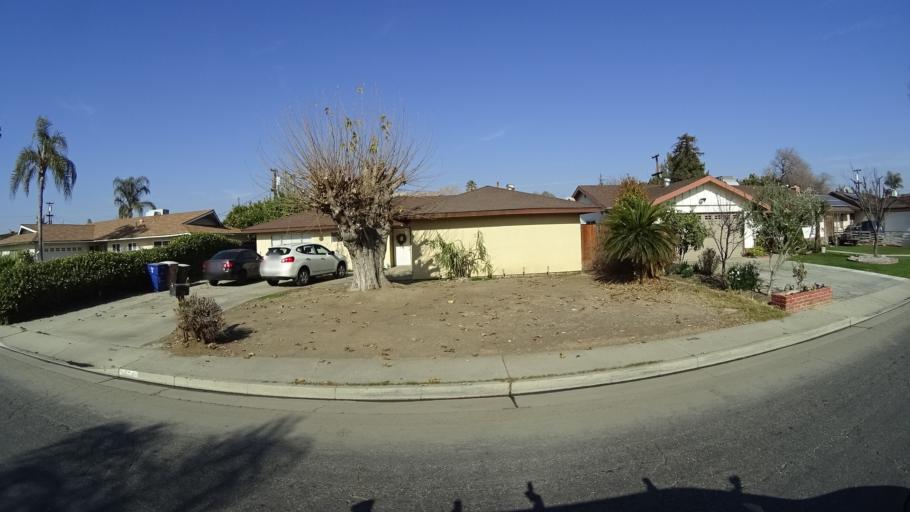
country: US
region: California
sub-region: Kern County
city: Bakersfield
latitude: 35.3362
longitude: -119.0417
